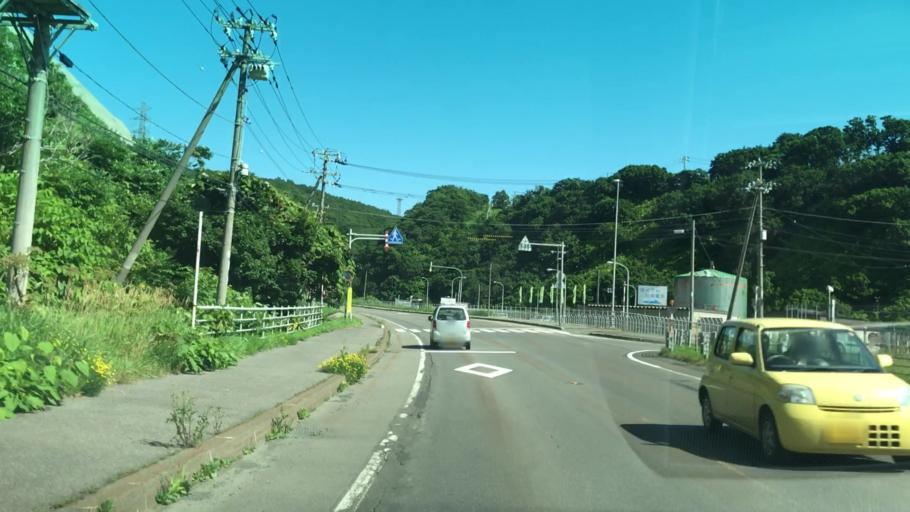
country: JP
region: Hokkaido
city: Iwanai
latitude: 43.0427
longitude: 140.5088
